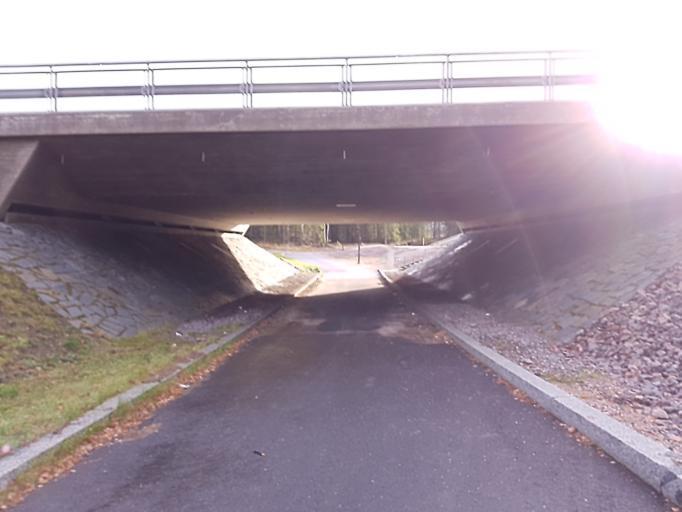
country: FI
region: Uusimaa
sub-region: Helsinki
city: Teekkarikylae
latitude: 60.2598
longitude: 24.8943
